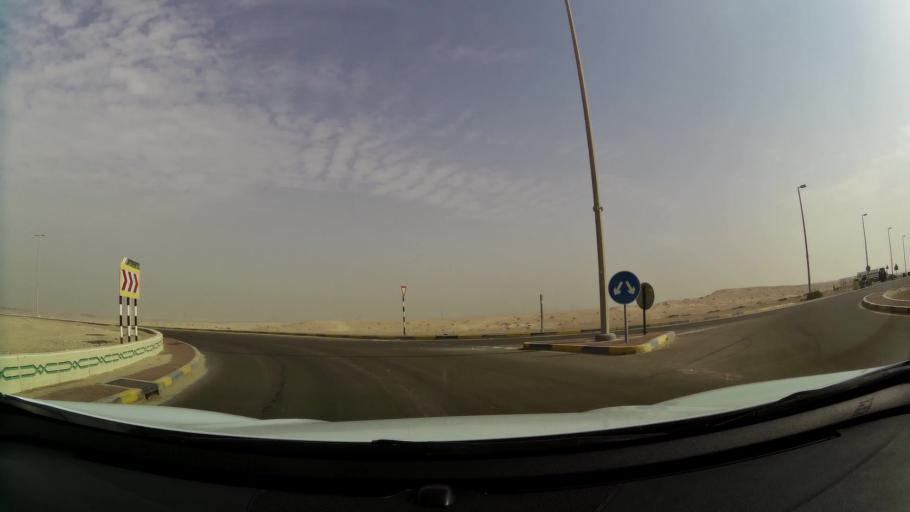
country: AE
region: Abu Dhabi
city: Abu Dhabi
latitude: 24.2806
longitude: 54.6846
